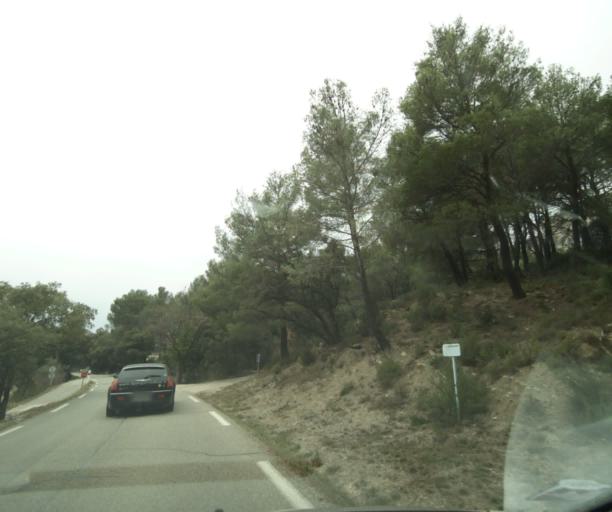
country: FR
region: Provence-Alpes-Cote d'Azur
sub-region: Departement des Bouches-du-Rhone
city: Chateauneuf-le-Rouge
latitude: 43.5558
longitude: 5.5908
